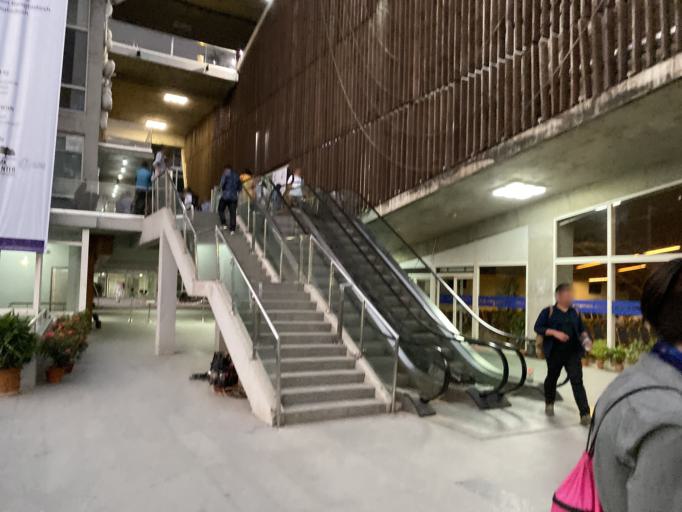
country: BD
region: Dhaka
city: Azimpur
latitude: 23.7593
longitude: 90.3852
